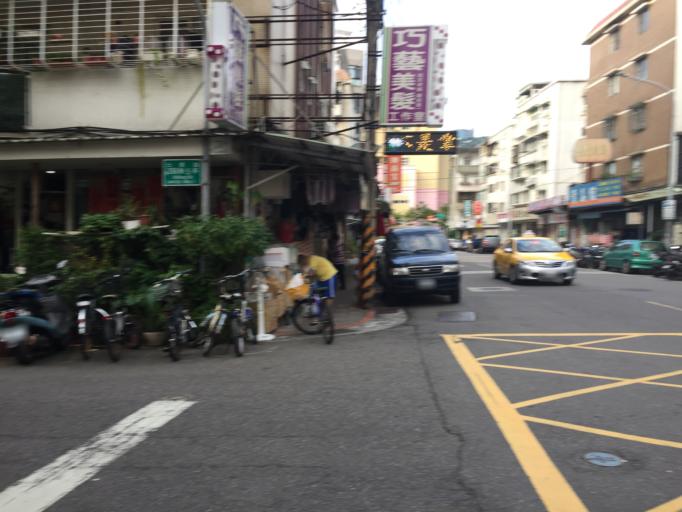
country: TW
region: Taipei
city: Taipei
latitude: 25.1123
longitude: 121.5375
